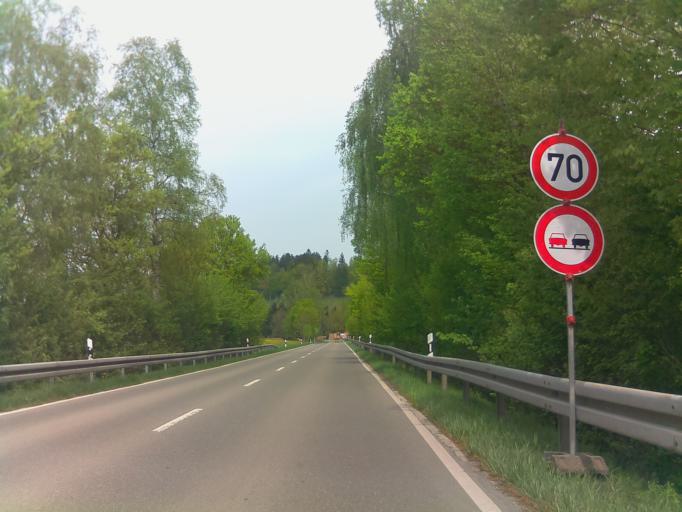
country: DE
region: Baden-Wuerttemberg
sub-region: Freiburg Region
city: Deisslingen
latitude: 48.1311
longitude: 8.6279
